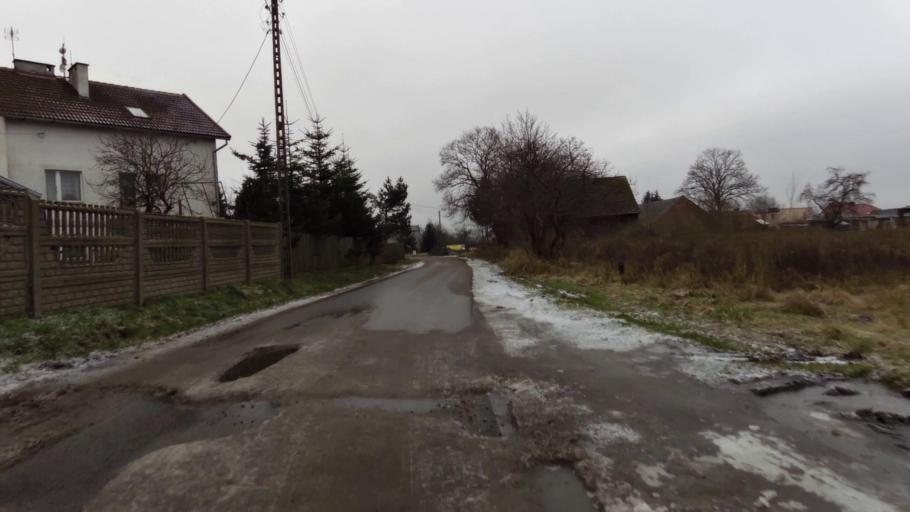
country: PL
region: West Pomeranian Voivodeship
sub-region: Powiat szczecinecki
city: Szczecinek
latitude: 53.6519
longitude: 16.6341
